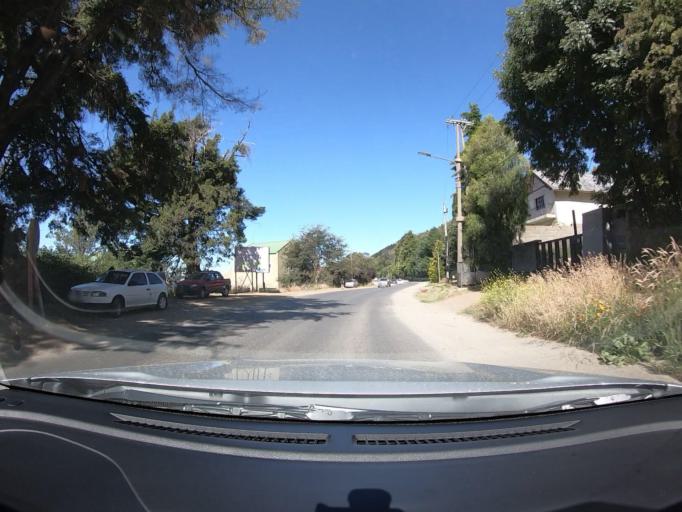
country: AR
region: Rio Negro
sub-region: Departamento de Bariloche
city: San Carlos de Bariloche
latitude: -41.1319
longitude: -71.3357
